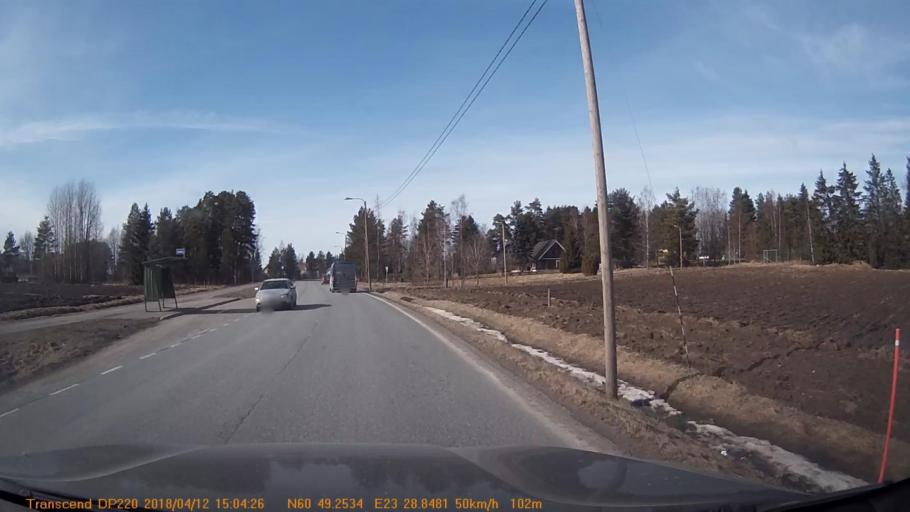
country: FI
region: Haeme
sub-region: Forssa
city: Jokioinen
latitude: 60.8211
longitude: 23.4806
